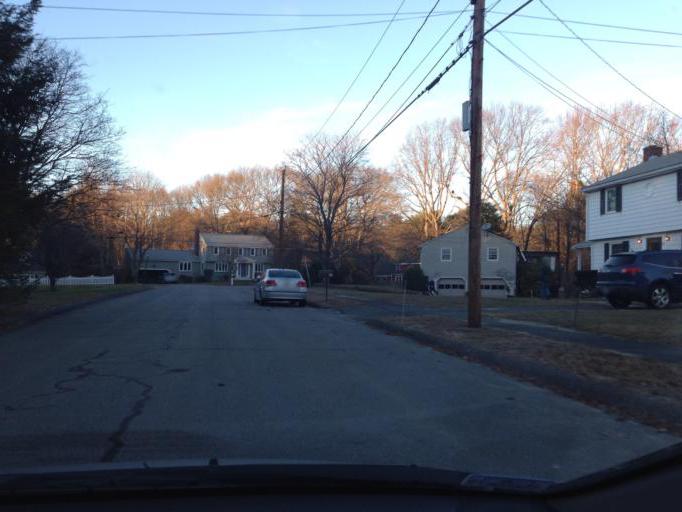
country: US
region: Massachusetts
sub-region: Middlesex County
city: Concord
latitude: 42.4751
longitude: -71.3223
